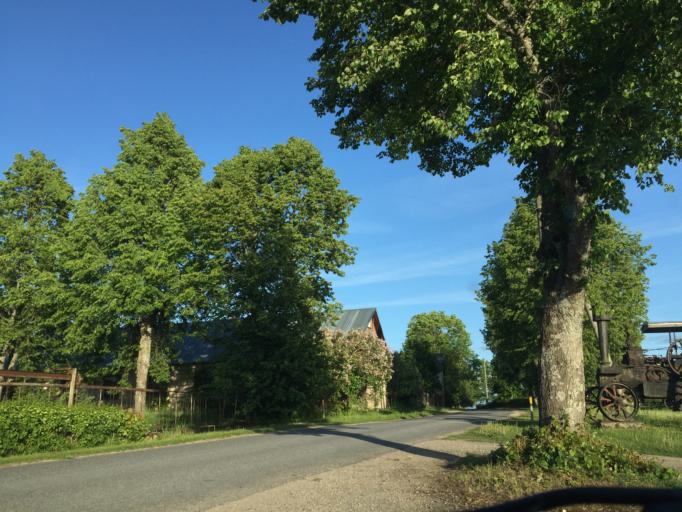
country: LV
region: Koceni
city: Koceni
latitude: 57.4779
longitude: 25.2404
